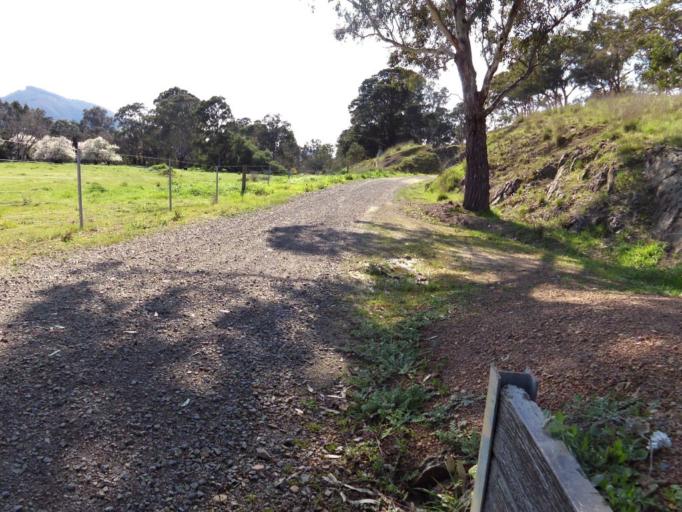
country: AU
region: Victoria
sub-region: Murrindindi
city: Alexandra
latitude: -37.1692
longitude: 145.5395
